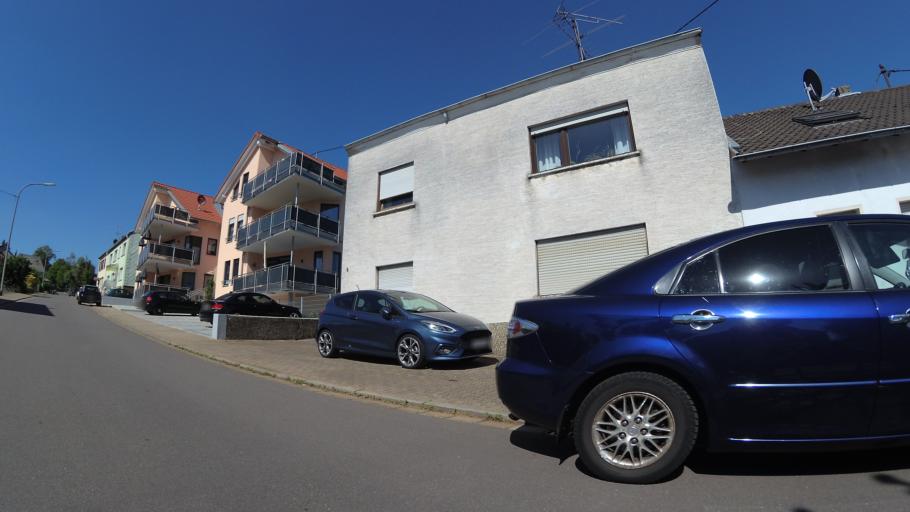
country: DE
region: Saarland
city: Saarwellingen
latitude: 49.3534
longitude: 6.8126
